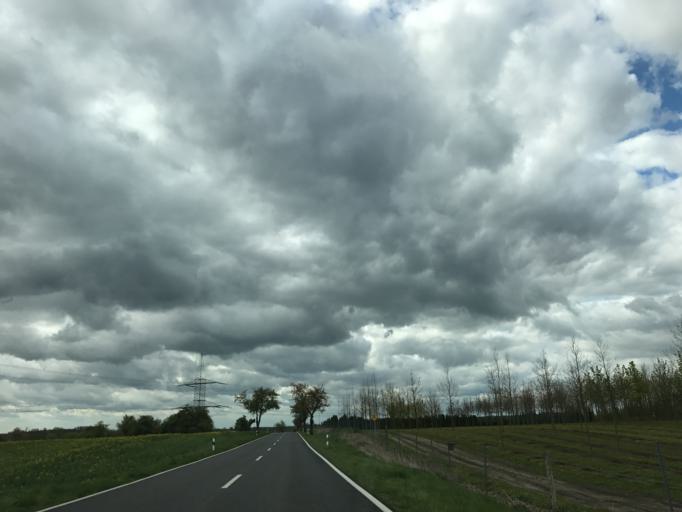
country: DE
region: Brandenburg
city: Pawesin
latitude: 52.5624
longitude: 12.7688
